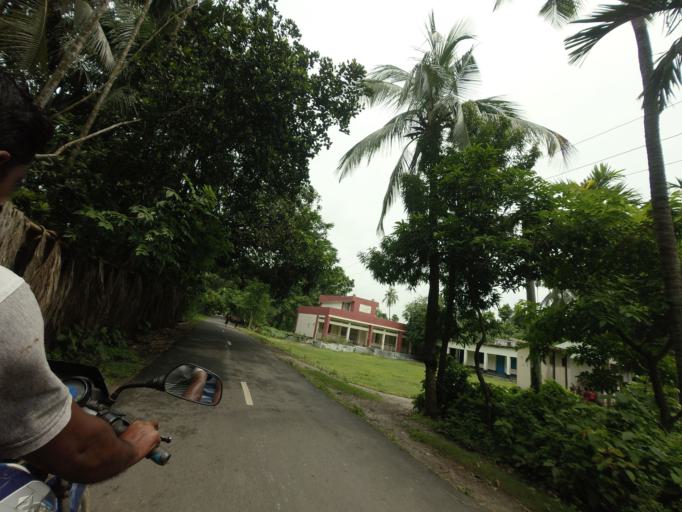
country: BD
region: Khulna
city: Kalia
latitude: 23.0882
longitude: 89.6611
